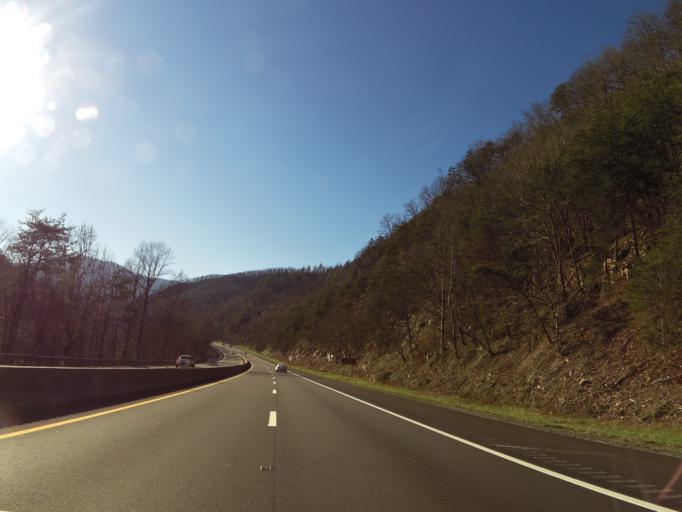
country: US
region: Tennessee
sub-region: Cocke County
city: Newport
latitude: 35.8295
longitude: -83.1833
